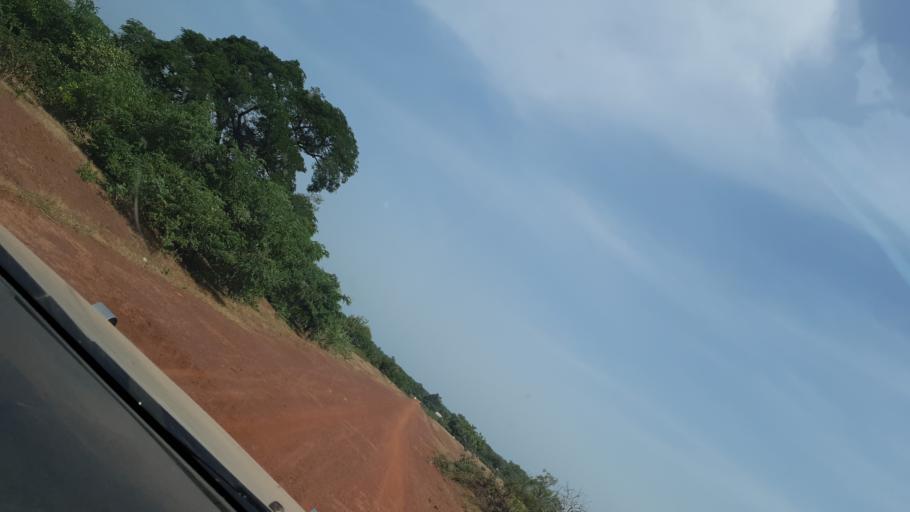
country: ML
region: Koulikoro
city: Dioila
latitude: 12.4732
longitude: -6.1854
